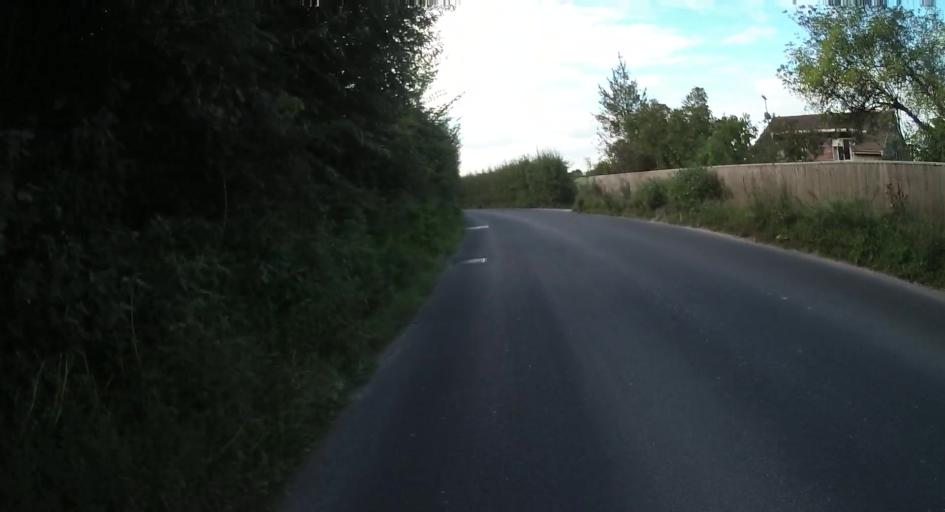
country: GB
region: England
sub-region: Isle of Wight
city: Newport
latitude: 50.6799
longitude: -1.3085
